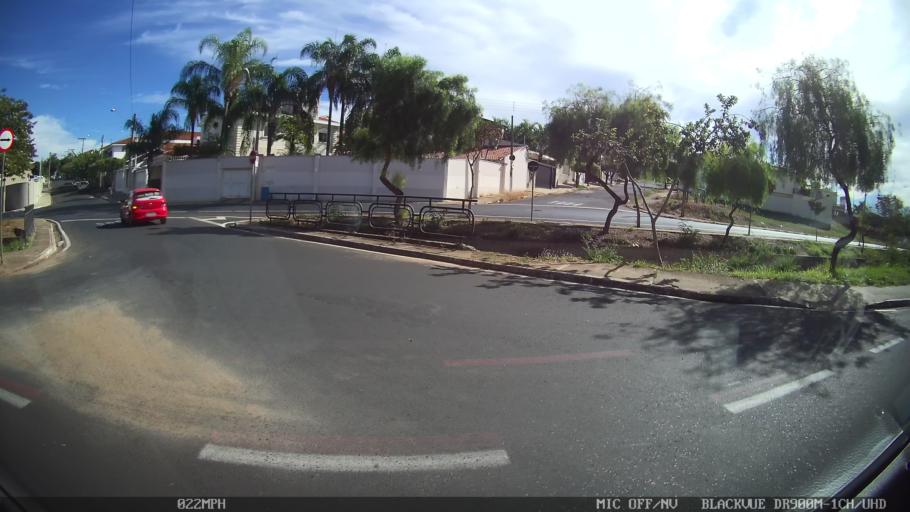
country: BR
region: Sao Paulo
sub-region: Catanduva
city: Catanduva
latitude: -21.1286
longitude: -48.9626
